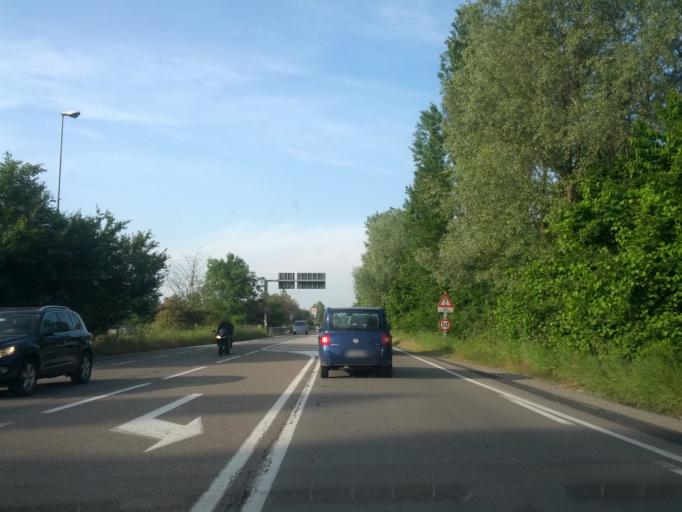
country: IT
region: Emilia-Romagna
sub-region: Provincia di Reggio Emilia
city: Bagnolo in Piano
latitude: 44.7683
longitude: 10.6653
